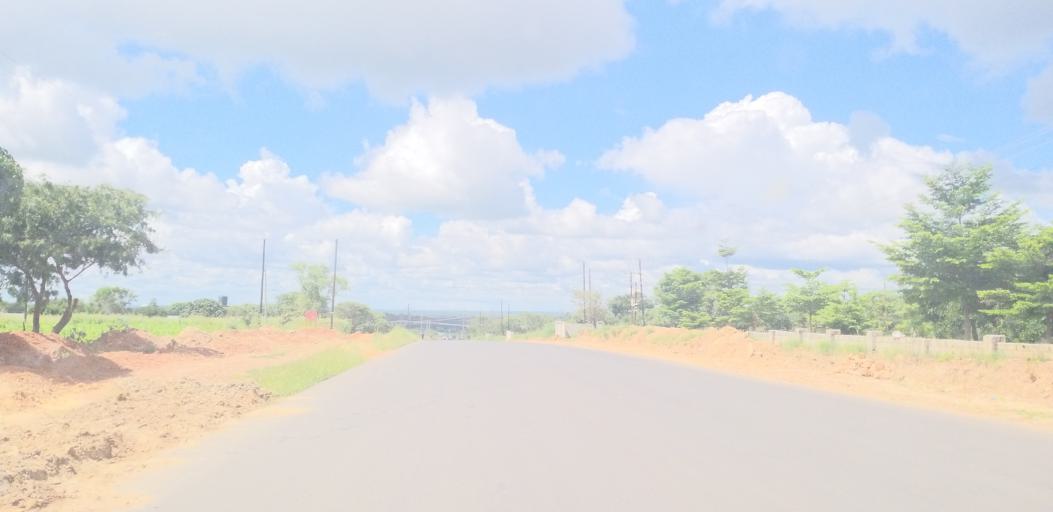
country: ZM
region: Lusaka
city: Lusaka
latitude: -15.3504
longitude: 28.3257
